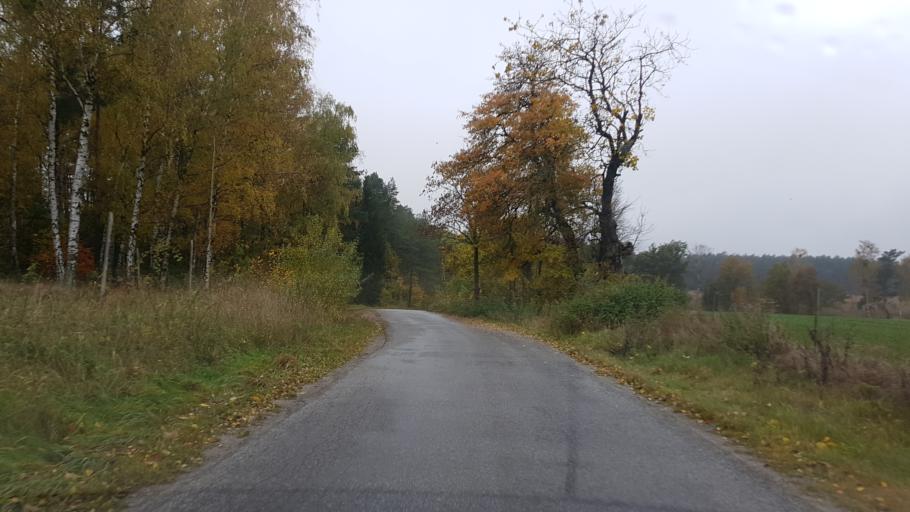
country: PL
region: West Pomeranian Voivodeship
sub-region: Powiat gryfinski
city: Chojna
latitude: 53.0549
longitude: 14.5143
